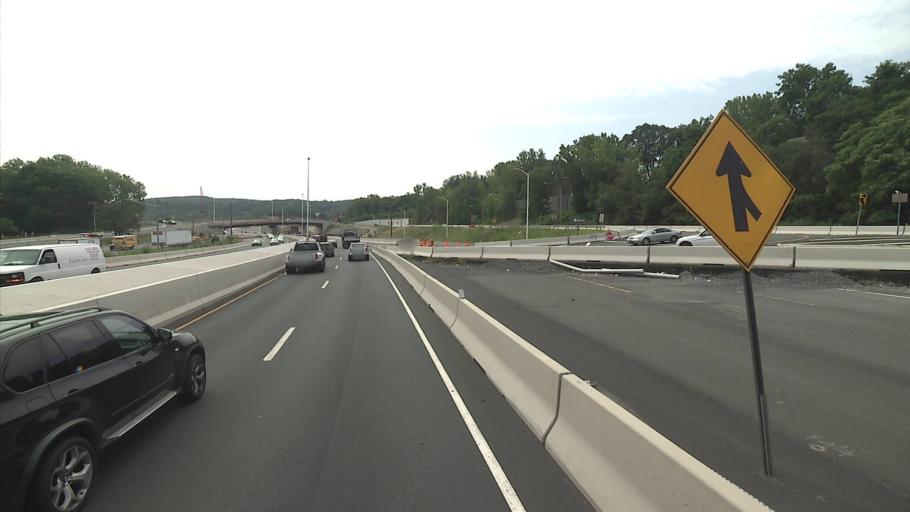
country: US
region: Connecticut
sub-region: New Haven County
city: Waterbury
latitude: 41.5439
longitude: -73.0255
